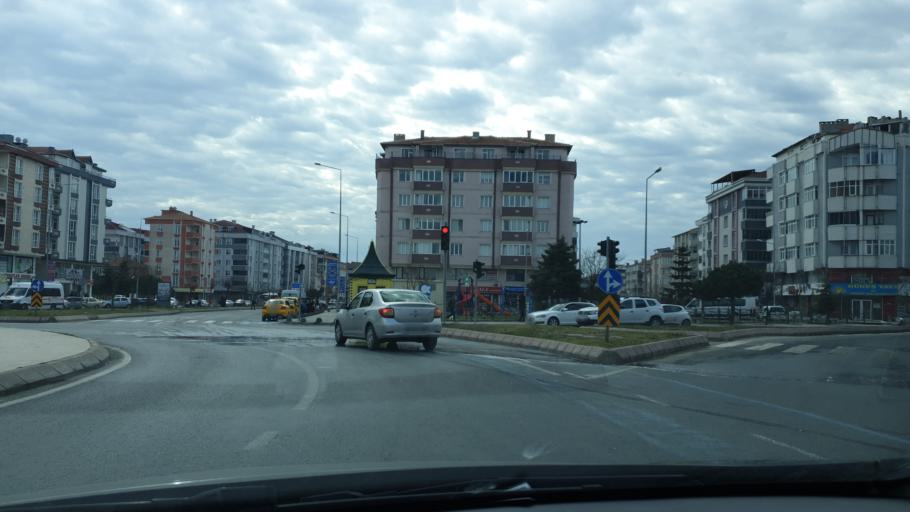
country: TR
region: Tekirdag
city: Cerkezkoey
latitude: 41.2882
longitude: 27.9903
